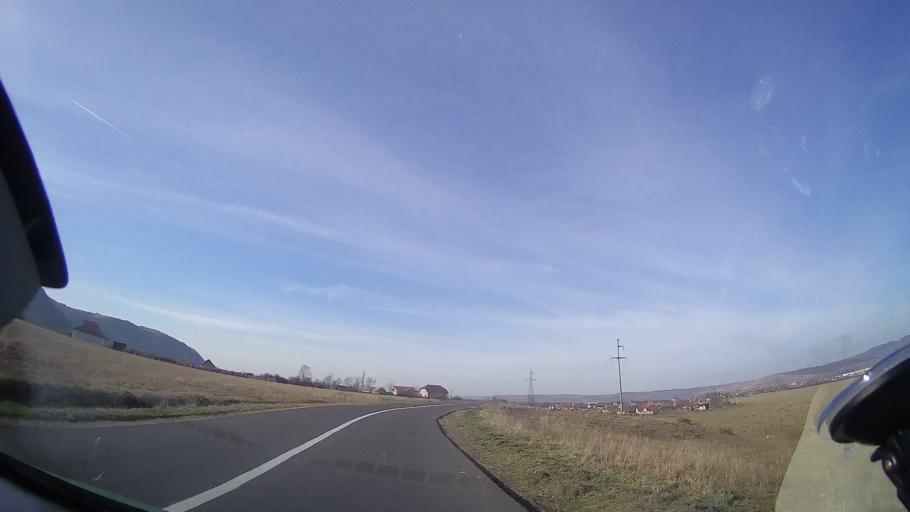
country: RO
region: Bihor
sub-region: Comuna Astileu
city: Astileu
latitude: 47.0249
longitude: 22.4055
